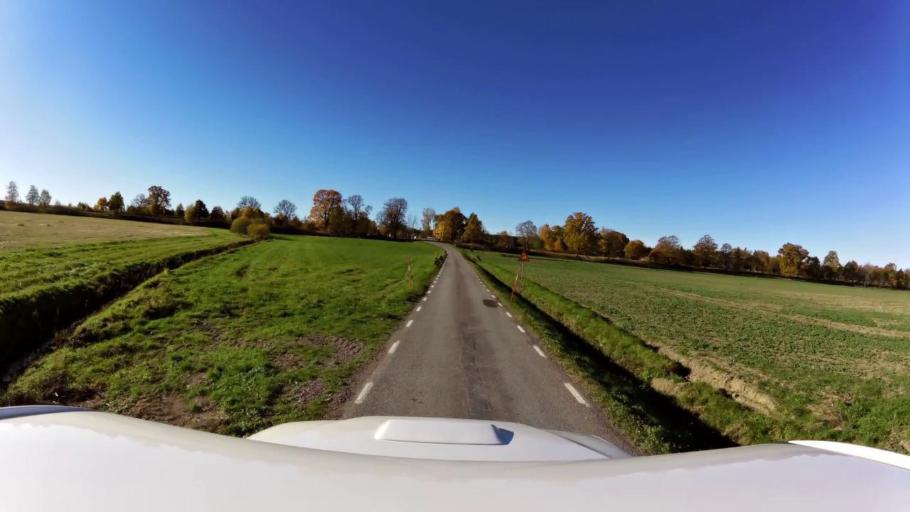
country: SE
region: OEstergoetland
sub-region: Linkopings Kommun
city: Ljungsbro
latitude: 58.5341
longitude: 15.3947
